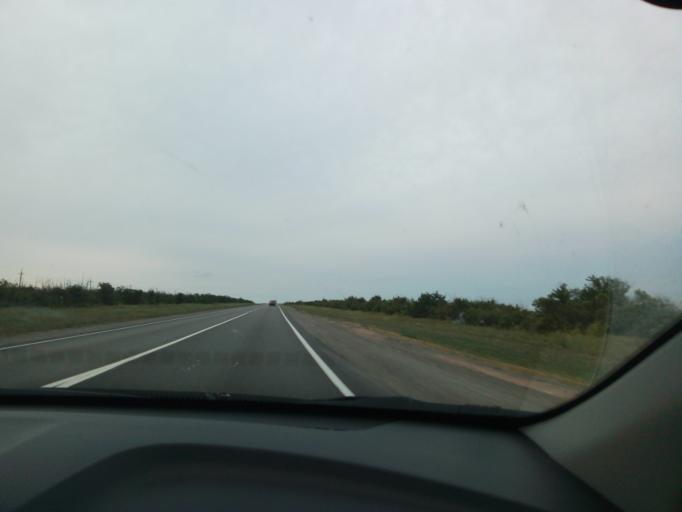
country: RU
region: Volgograd
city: Primorsk
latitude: 49.2011
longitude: 44.8939
